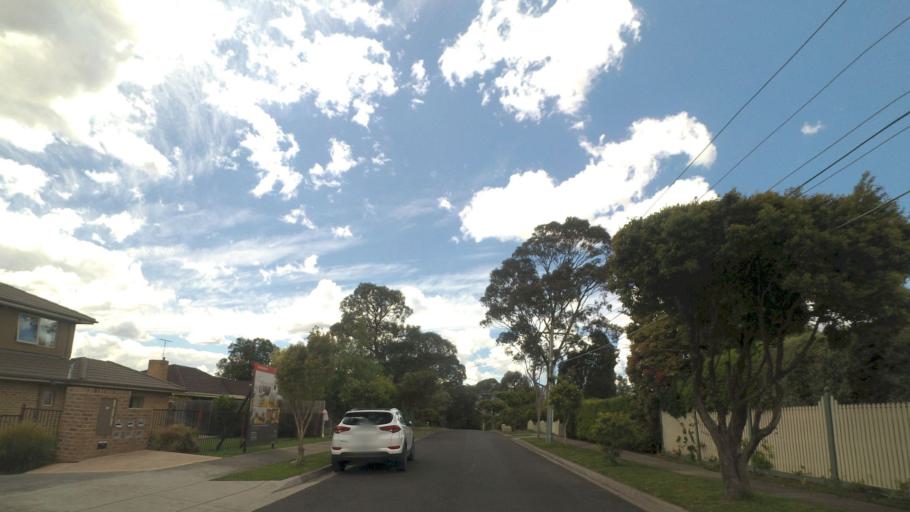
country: AU
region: Victoria
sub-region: Maroondah
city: Croydon South
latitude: -37.8163
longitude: 145.2768
